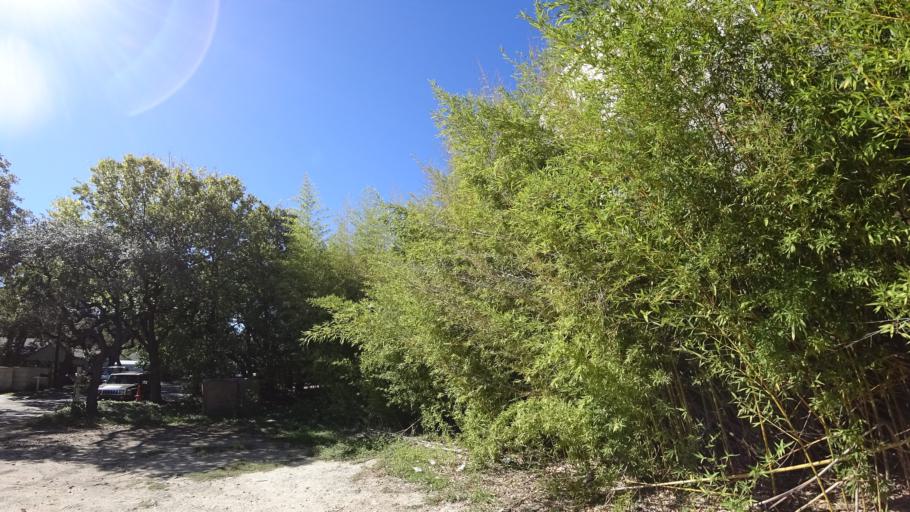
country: US
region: Texas
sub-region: Travis County
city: Austin
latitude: 30.2443
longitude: -97.7629
